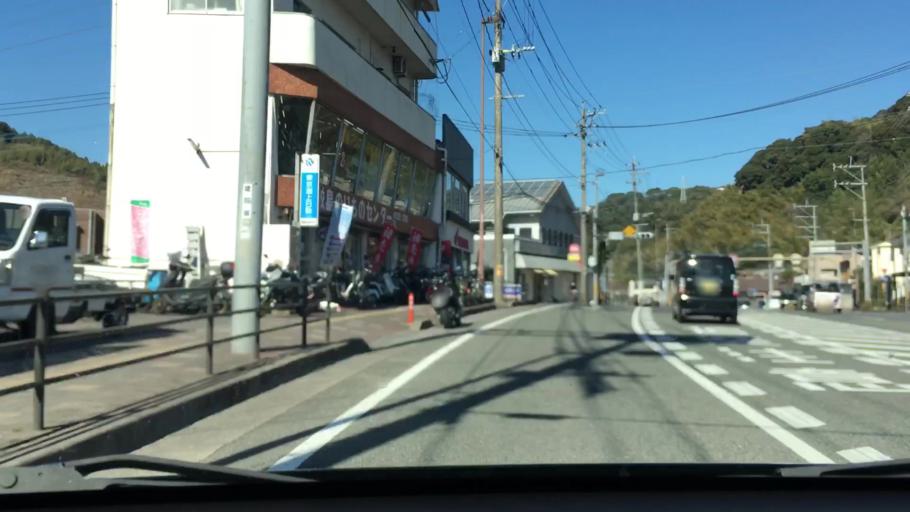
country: JP
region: Kagoshima
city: Kagoshima-shi
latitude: 31.6277
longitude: 130.5251
